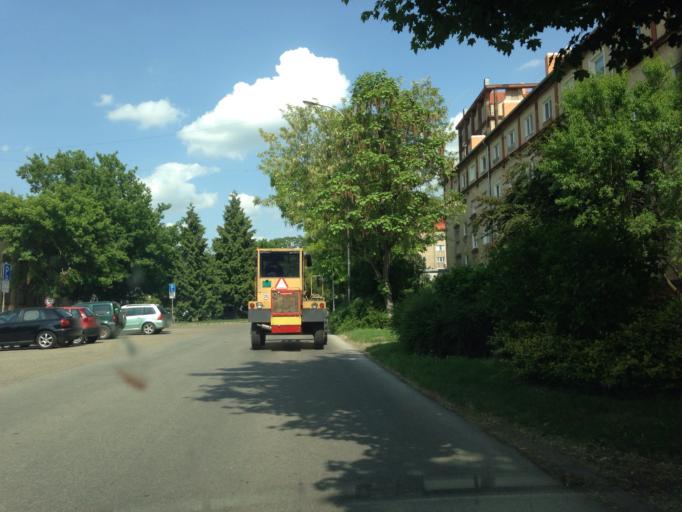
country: SK
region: Nitriansky
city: Komarno
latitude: 47.7573
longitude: 18.1313
